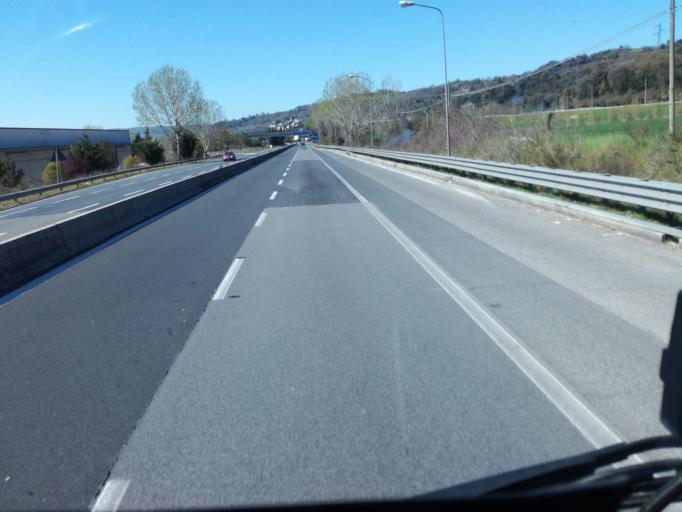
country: IT
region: Umbria
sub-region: Provincia di Terni
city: Fornole
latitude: 42.4849
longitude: 12.4520
